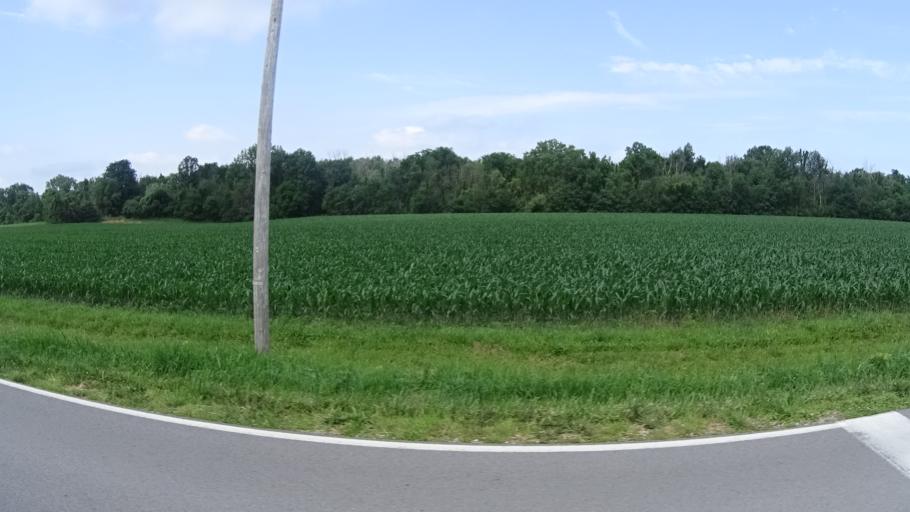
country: US
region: Ohio
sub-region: Lorain County
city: Vermilion
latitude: 41.3962
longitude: -82.4063
